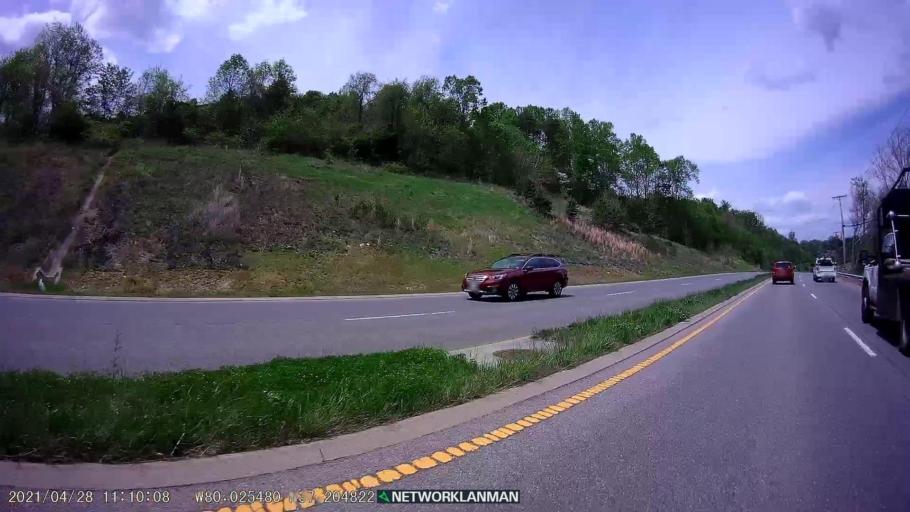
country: US
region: Virginia
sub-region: Roanoke County
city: Cave Spring
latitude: 37.2050
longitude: -80.0255
